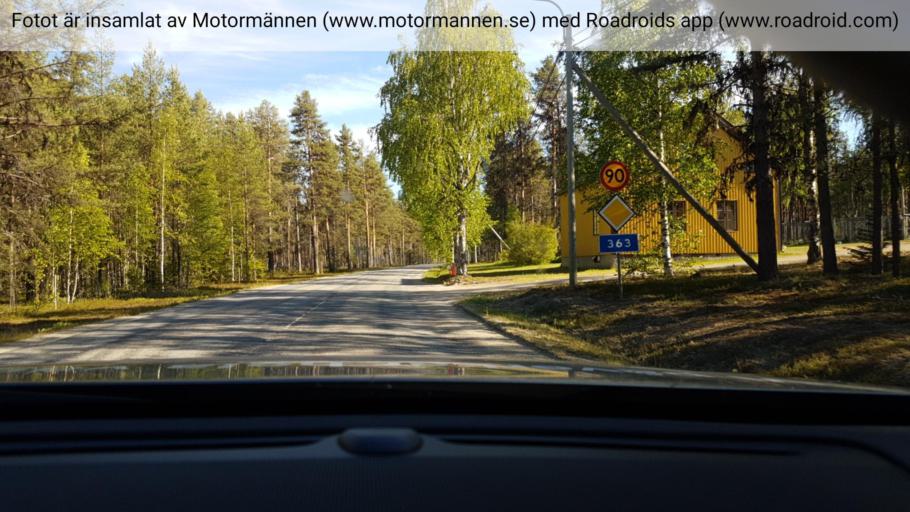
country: SE
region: Vaesterbotten
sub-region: Norsjo Kommun
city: Norsjoe
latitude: 64.6627
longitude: 19.2696
